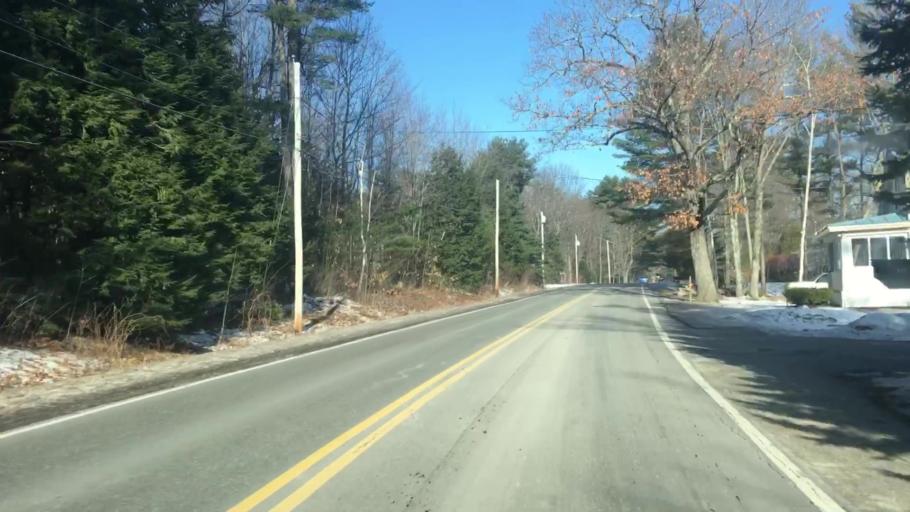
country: US
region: Maine
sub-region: Androscoggin County
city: Auburn
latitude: 44.1155
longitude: -70.2704
